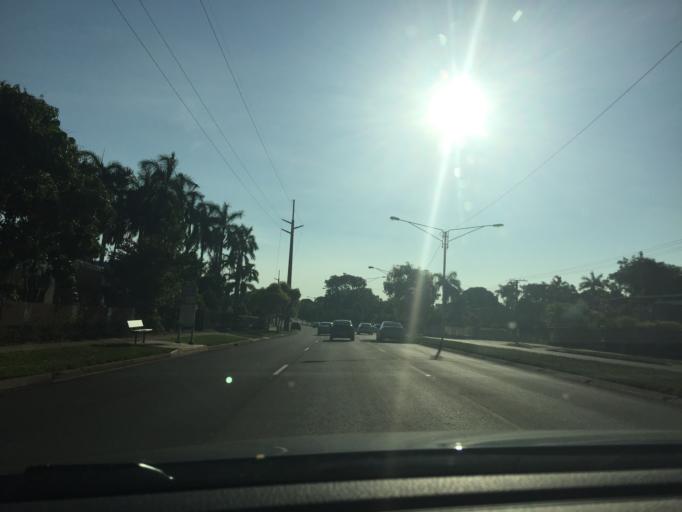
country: AU
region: Northern Territory
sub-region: Darwin
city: Nightcliff
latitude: -12.3836
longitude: 130.8713
